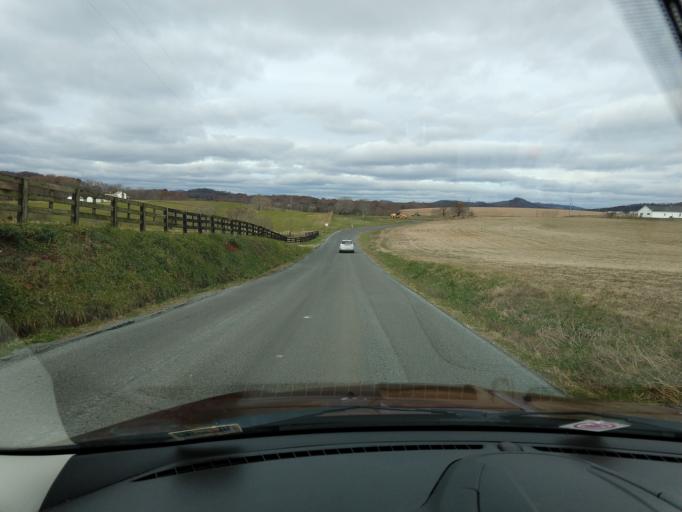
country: US
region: Virginia
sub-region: Franklin County
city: North Shore
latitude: 37.2268
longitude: -79.6790
